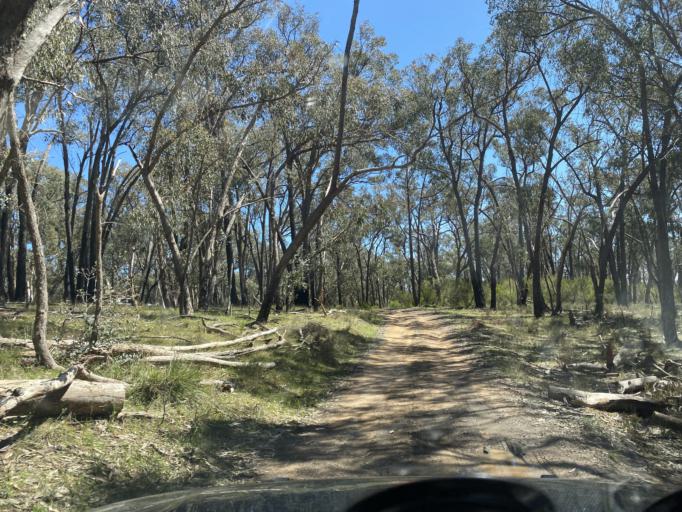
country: AU
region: Victoria
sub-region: Benalla
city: Benalla
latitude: -36.7047
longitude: 146.1547
